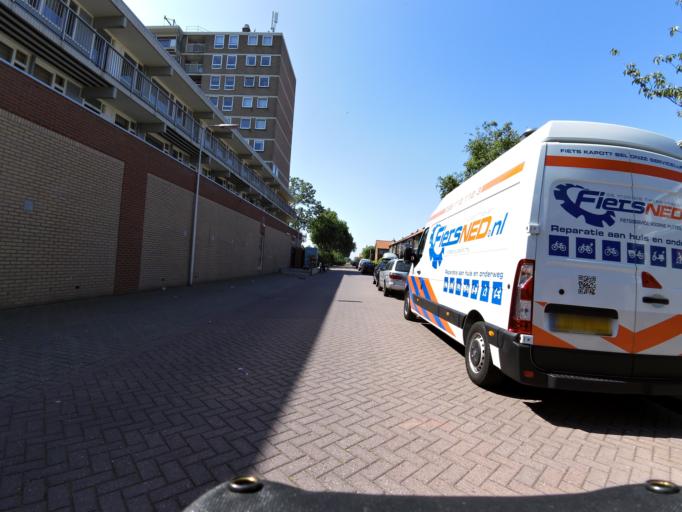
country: NL
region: South Holland
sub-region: Gemeente Brielle
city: Brielle
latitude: 51.8999
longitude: 4.1542
